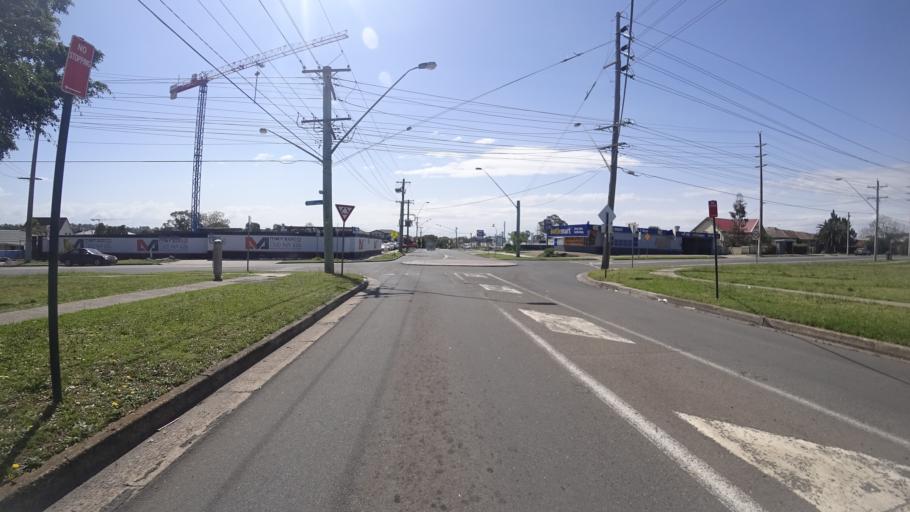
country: AU
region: New South Wales
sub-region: Liverpool
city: Miller
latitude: -33.9323
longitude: 150.8959
